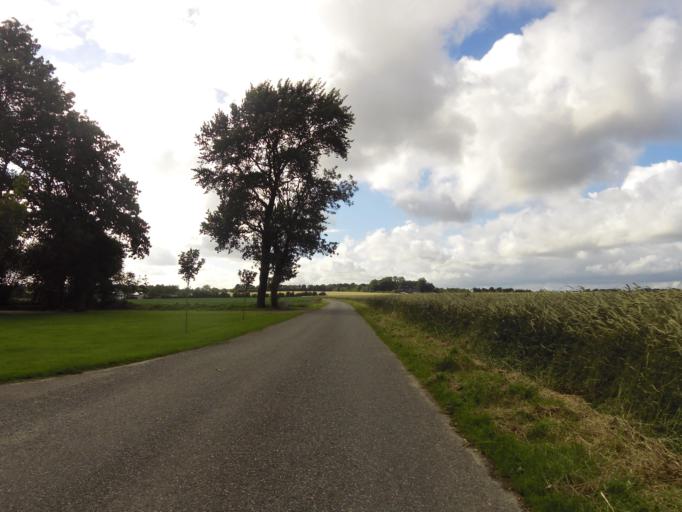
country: DK
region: South Denmark
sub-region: Tonder Kommune
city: Toftlund
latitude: 55.1313
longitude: 9.0760
